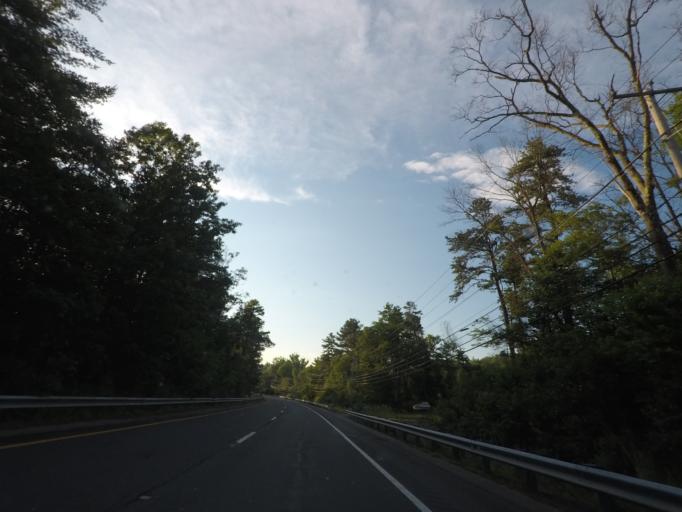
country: US
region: Massachusetts
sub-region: Hampden County
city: Brimfield
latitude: 42.1303
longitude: -72.2547
